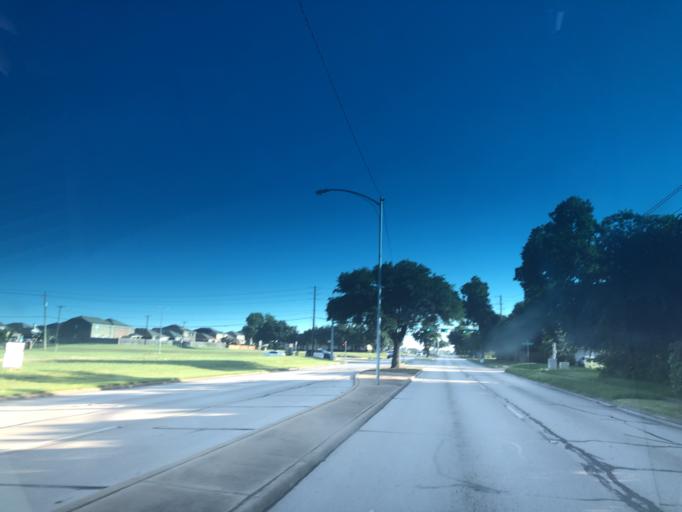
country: US
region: Texas
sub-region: Dallas County
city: Grand Prairie
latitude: 32.7044
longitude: -97.0155
